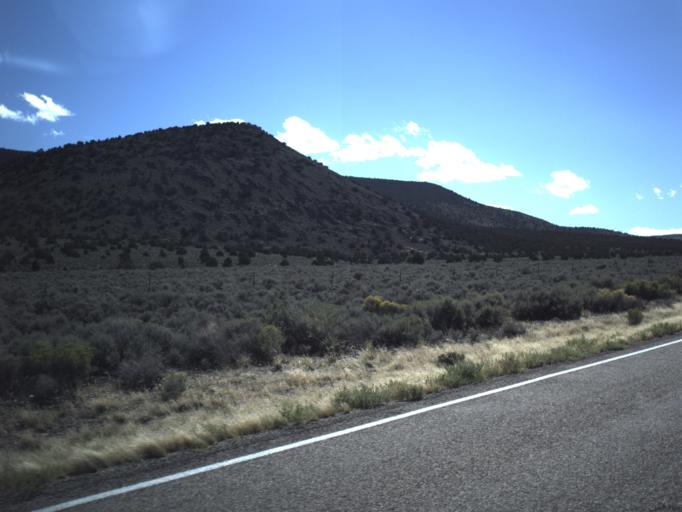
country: US
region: Utah
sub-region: Beaver County
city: Milford
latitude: 38.1428
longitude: -112.9600
